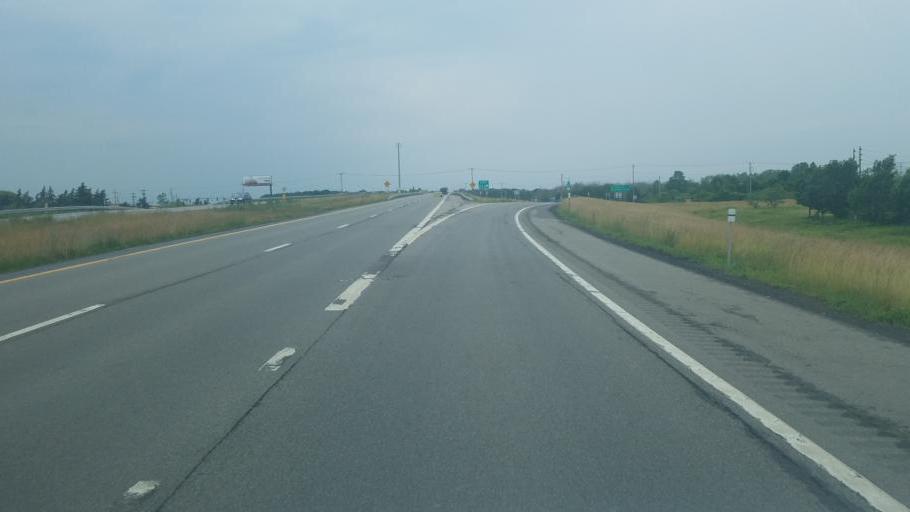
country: US
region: New York
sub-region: Niagara County
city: Niagara Falls
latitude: 43.1061
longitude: -78.9863
